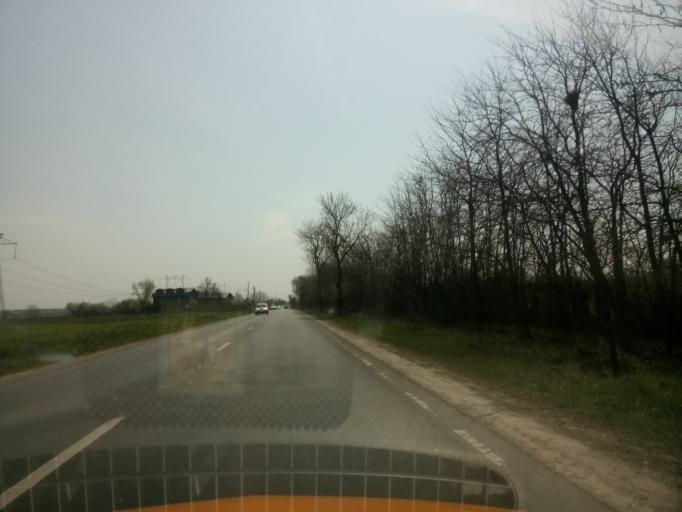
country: RO
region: Calarasi
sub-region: Comuna Frumusani
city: Frumusani
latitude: 44.3188
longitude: 26.2725
